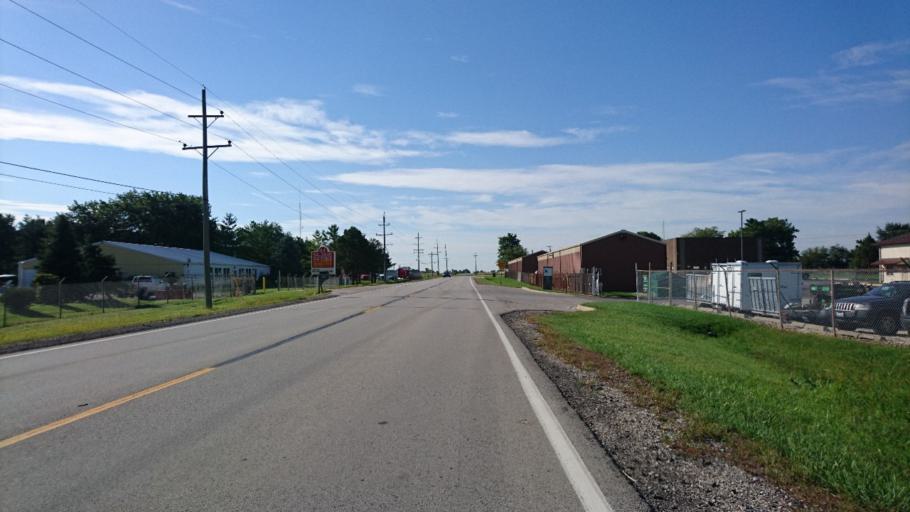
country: US
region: Illinois
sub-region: Will County
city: Ingalls Park
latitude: 41.4776
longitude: -88.0225
